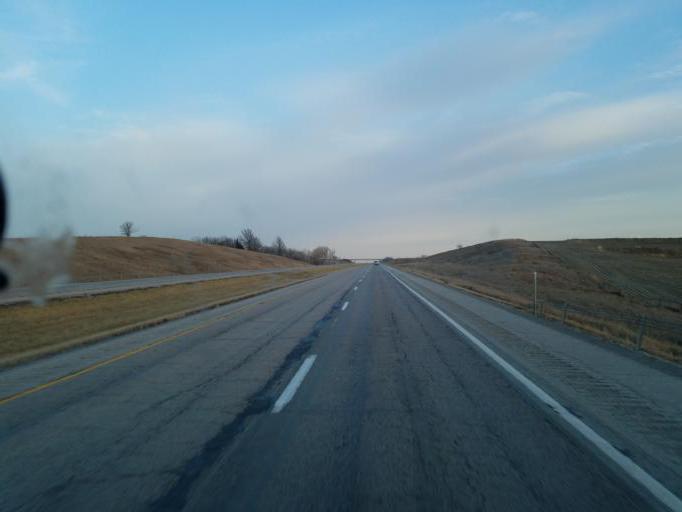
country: US
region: Iowa
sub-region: Harrison County
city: Missouri Valley
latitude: 41.4992
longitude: -95.7756
